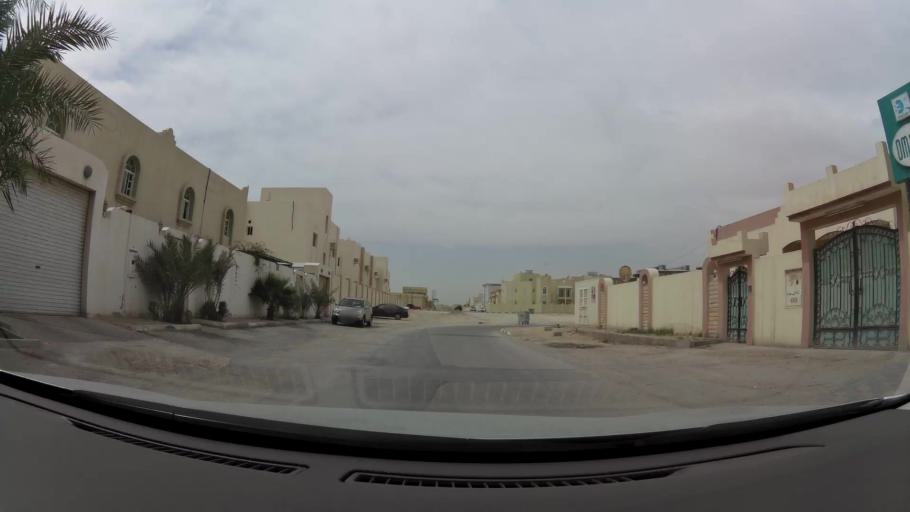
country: QA
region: Baladiyat ar Rayyan
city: Ar Rayyan
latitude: 25.2314
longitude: 51.4537
